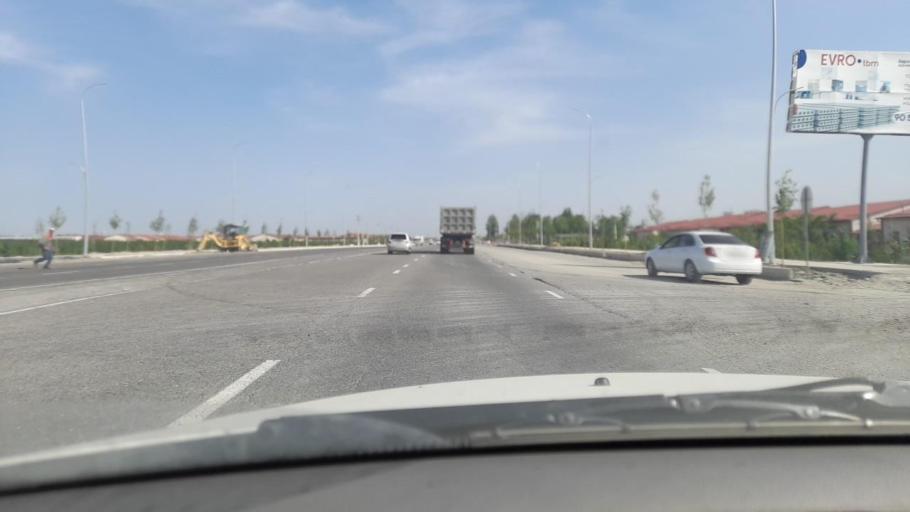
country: UZ
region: Samarqand
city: Daxbet
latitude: 39.7369
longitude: 66.9307
